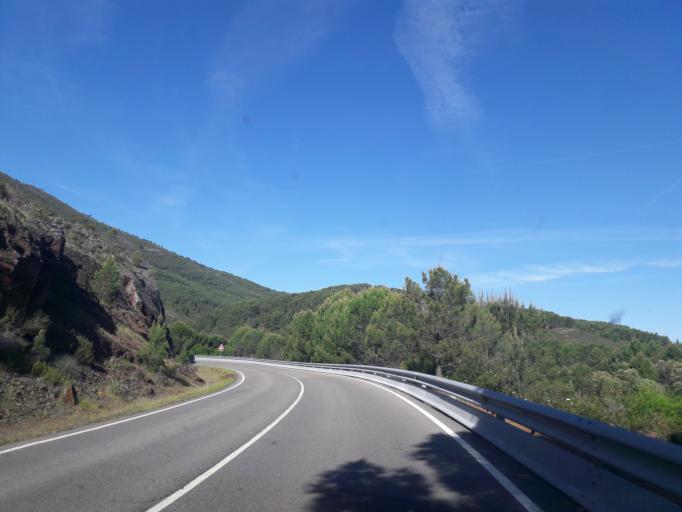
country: ES
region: Castille and Leon
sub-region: Provincia de Salamanca
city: Herguijuela de la Sierra
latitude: 40.4078
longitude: -6.0890
